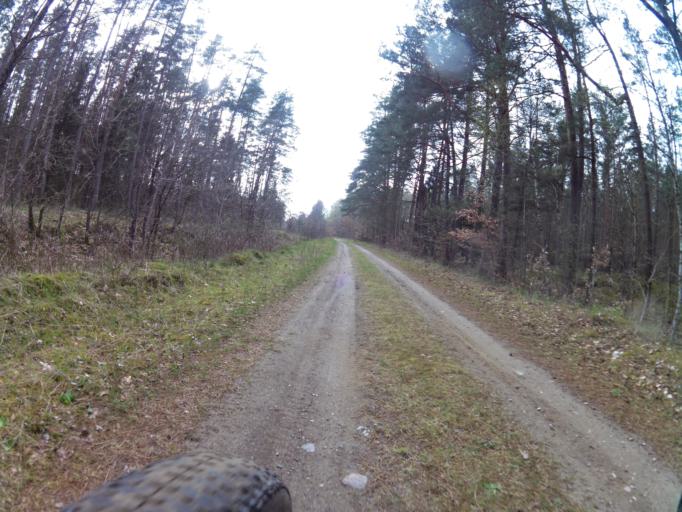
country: PL
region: West Pomeranian Voivodeship
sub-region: Powiat slawienski
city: Slawno
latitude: 54.3286
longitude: 16.7472
